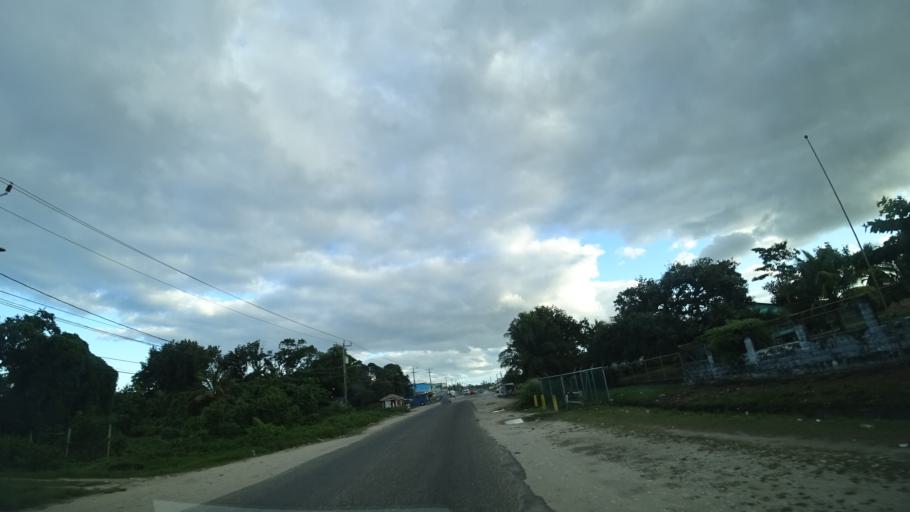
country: BZ
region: Belize
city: Belize City
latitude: 17.5560
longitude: -88.3096
